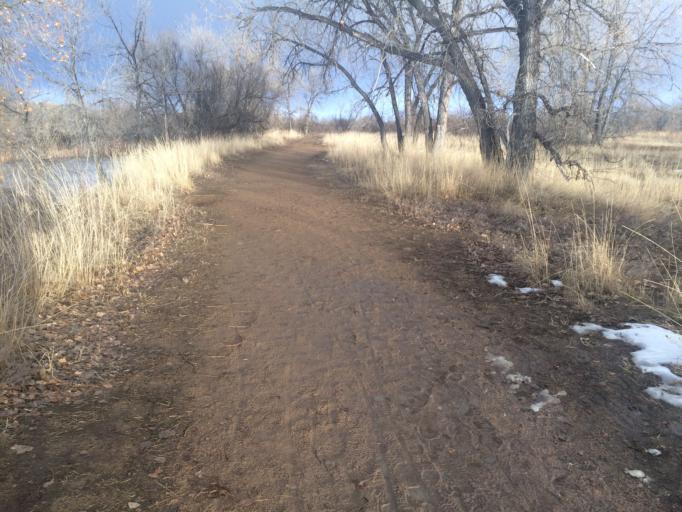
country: US
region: Colorado
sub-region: Boulder County
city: Gunbarrel
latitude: 40.0400
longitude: -105.1895
